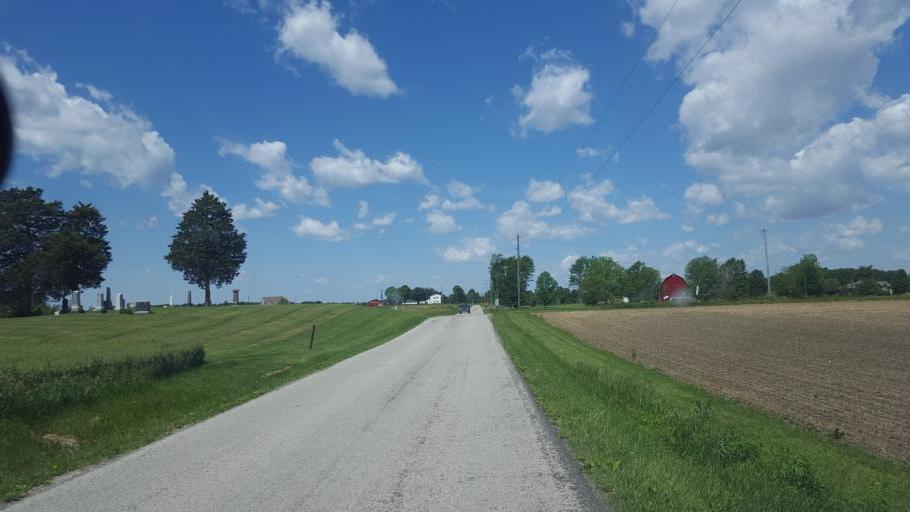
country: US
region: Ohio
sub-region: Richland County
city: Shelby
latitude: 40.8360
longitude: -82.6765
